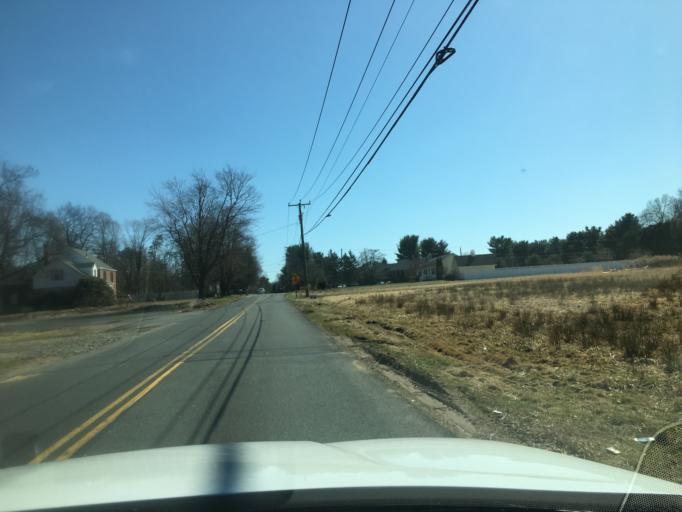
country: US
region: Connecticut
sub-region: Hartford County
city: East Hartford
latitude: 41.8085
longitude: -72.5777
